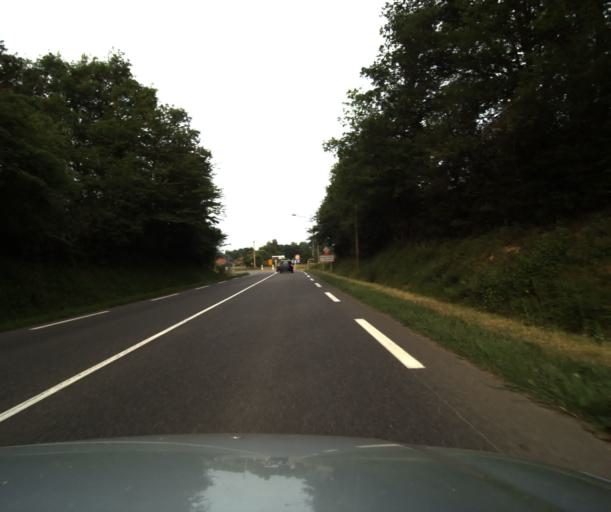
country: FR
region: Midi-Pyrenees
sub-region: Departement des Hautes-Pyrenees
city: Rabastens-de-Bigorre
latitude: 43.3914
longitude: 0.1625
